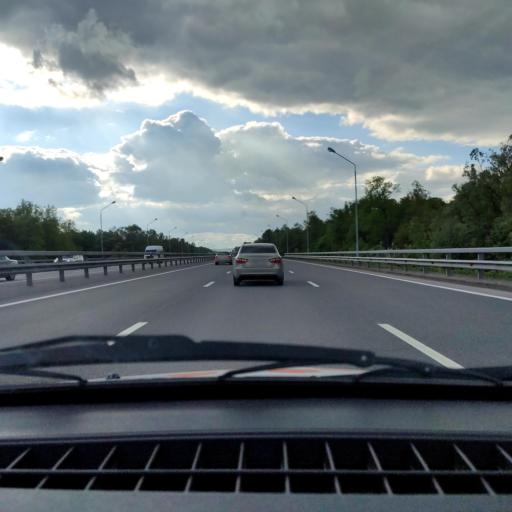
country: RU
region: Bashkortostan
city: Ufa
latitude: 54.6600
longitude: 55.8879
